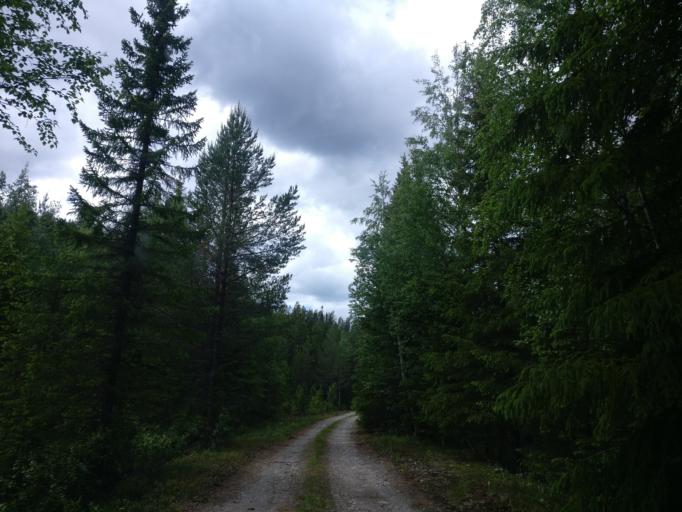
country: SE
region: Jaemtland
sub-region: Harjedalens Kommun
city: Sveg
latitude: 62.1950
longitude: 13.4165
